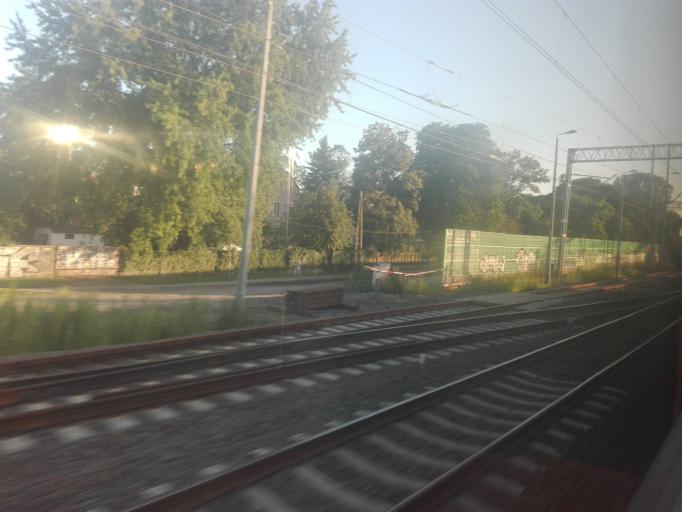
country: PL
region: Masovian Voivodeship
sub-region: Warszawa
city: Ursus
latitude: 52.2079
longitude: 20.9204
